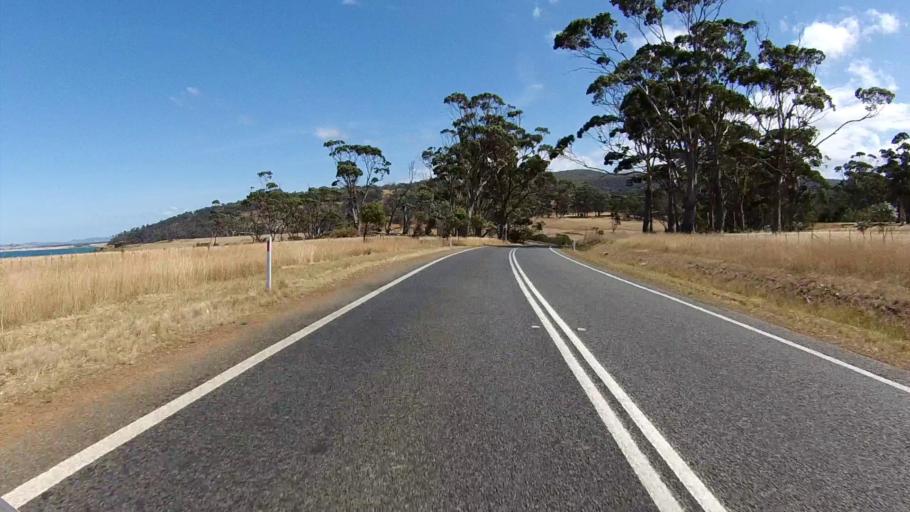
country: AU
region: Tasmania
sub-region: Sorell
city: Sorell
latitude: -42.2119
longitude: 148.0375
